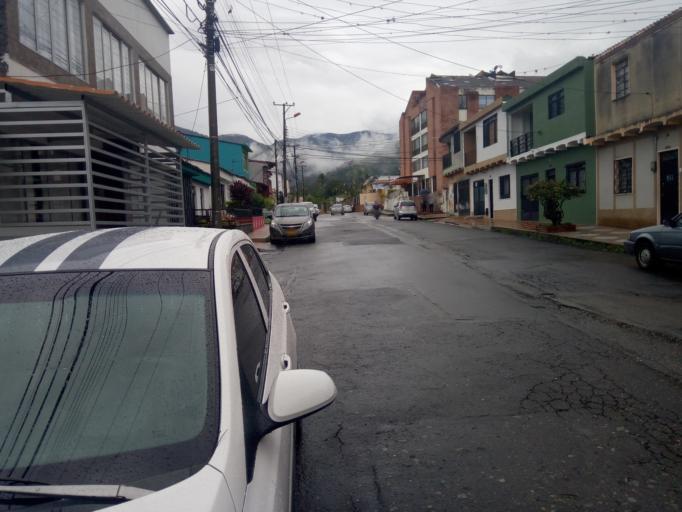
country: CO
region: Tolima
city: Ibague
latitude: 4.4516
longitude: -75.2459
